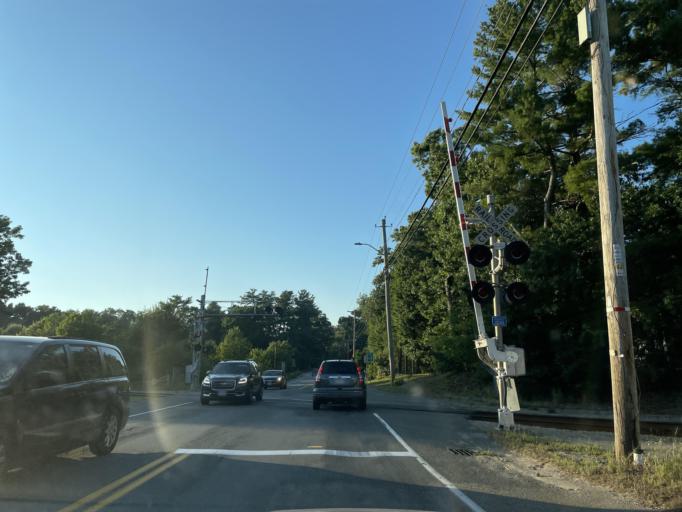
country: US
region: Massachusetts
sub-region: Plymouth County
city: Halifax
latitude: 42.0234
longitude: -70.8419
